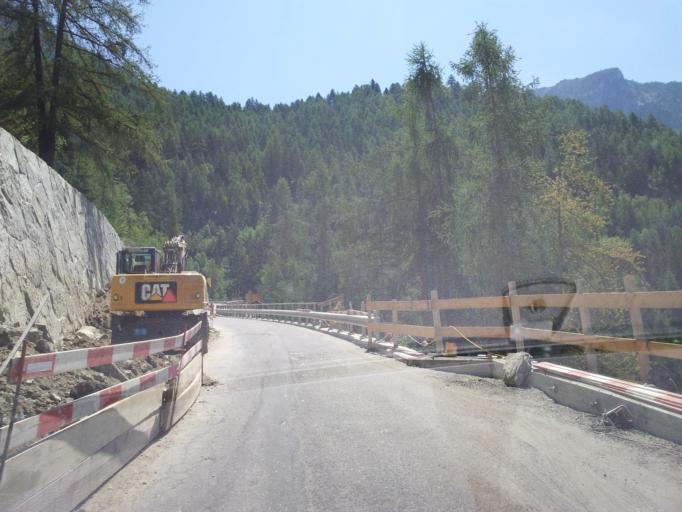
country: CH
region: Valais
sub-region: Visp District
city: Sankt Niklaus
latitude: 46.1854
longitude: 7.8173
